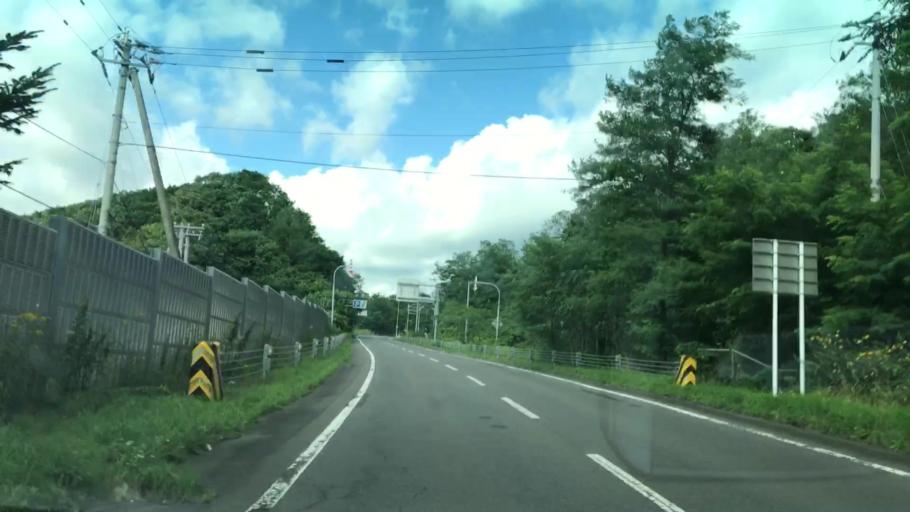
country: JP
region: Hokkaido
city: Muroran
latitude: 42.3666
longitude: 140.9537
